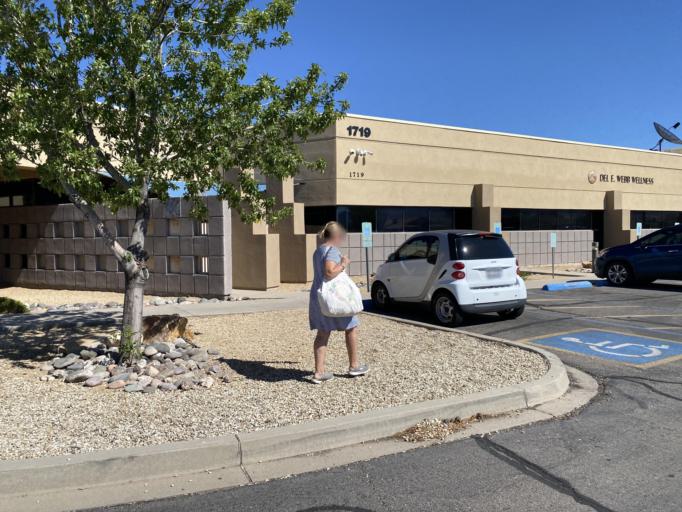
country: US
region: Arizona
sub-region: Mohave County
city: Kingman
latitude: 35.2190
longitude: -114.0393
